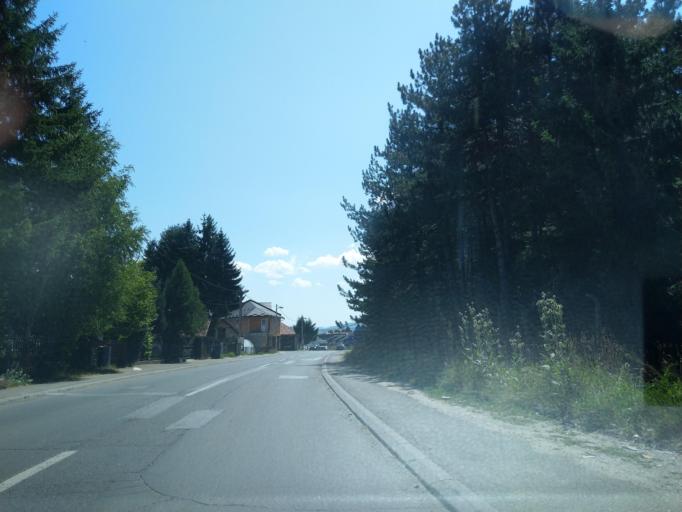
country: RS
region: Central Serbia
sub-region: Zlatiborski Okrug
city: Sjenica
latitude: 43.2763
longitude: 19.9953
